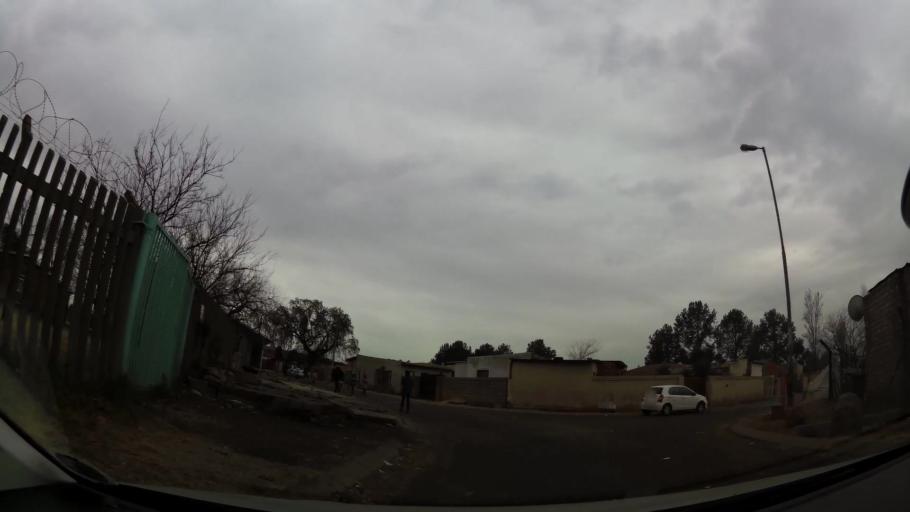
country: ZA
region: Gauteng
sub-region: City of Johannesburg Metropolitan Municipality
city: Soweto
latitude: -26.2528
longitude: 27.8724
